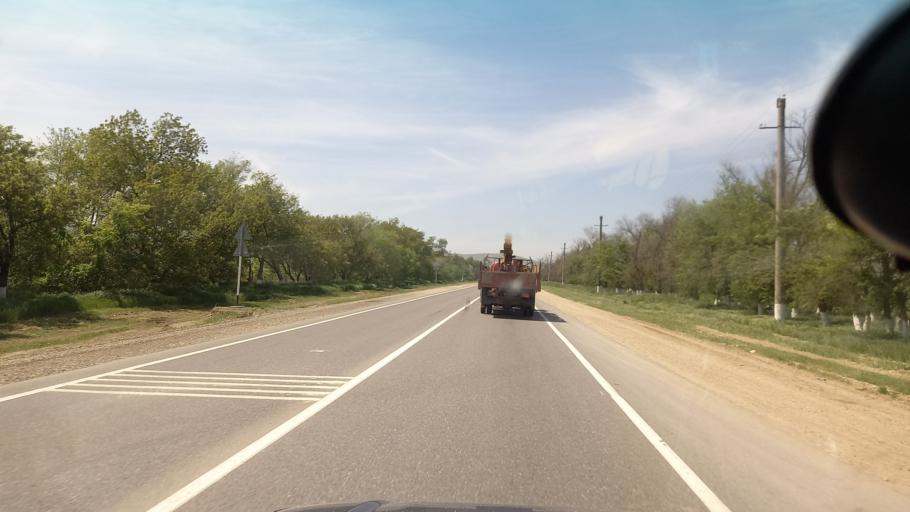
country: RU
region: Dagestan
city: Manas
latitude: 42.7079
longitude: 47.6876
